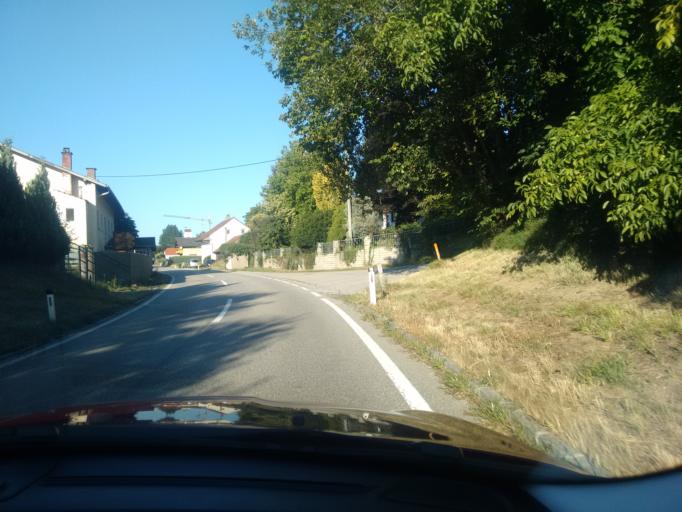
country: DE
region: Bavaria
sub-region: Upper Bavaria
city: Burghausen
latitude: 48.1663
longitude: 12.8558
